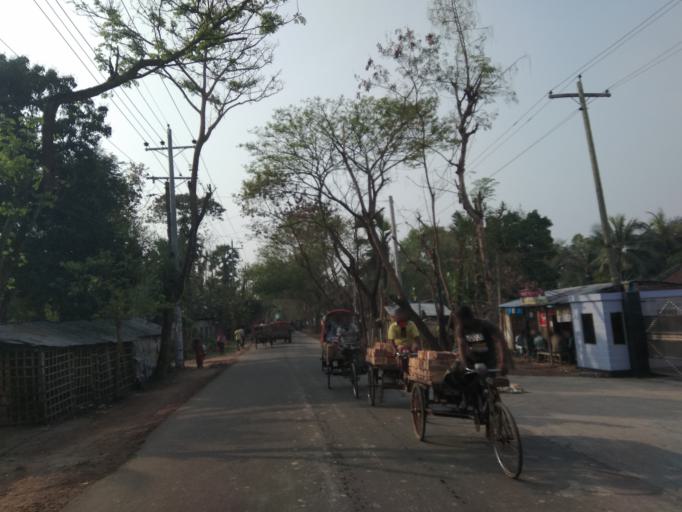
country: IN
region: West Bengal
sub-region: North 24 Parganas
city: Taki
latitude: 22.3266
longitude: 89.1054
